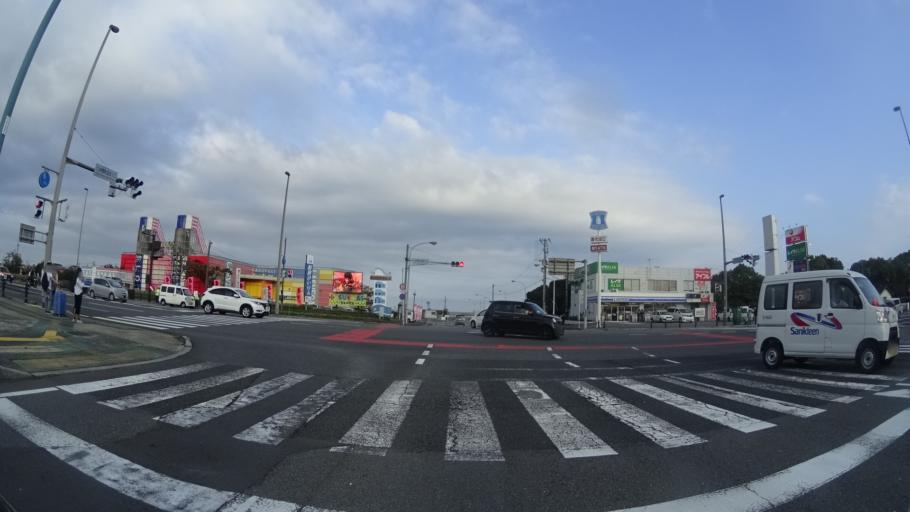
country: JP
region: Oita
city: Beppu
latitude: 33.3056
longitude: 131.5019
